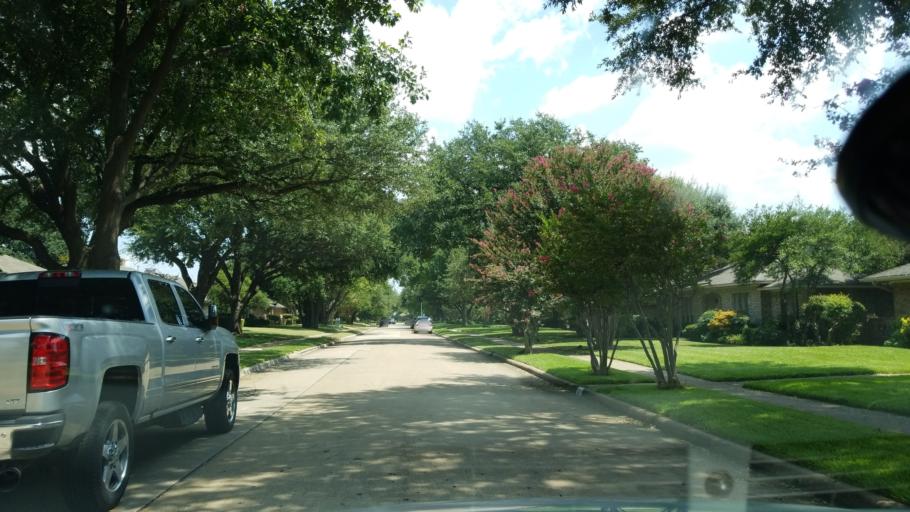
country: US
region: Texas
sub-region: Dallas County
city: Richardson
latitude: 32.9285
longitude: -96.7224
